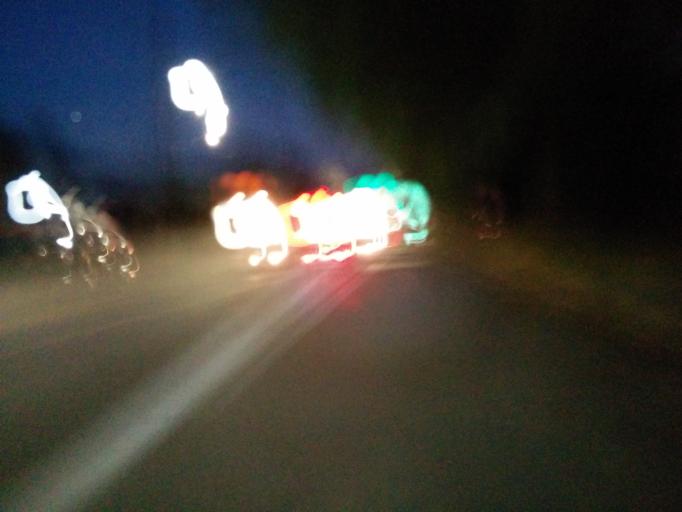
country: US
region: Washington
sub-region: King County
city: Seattle
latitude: 47.6721
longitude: -122.3663
